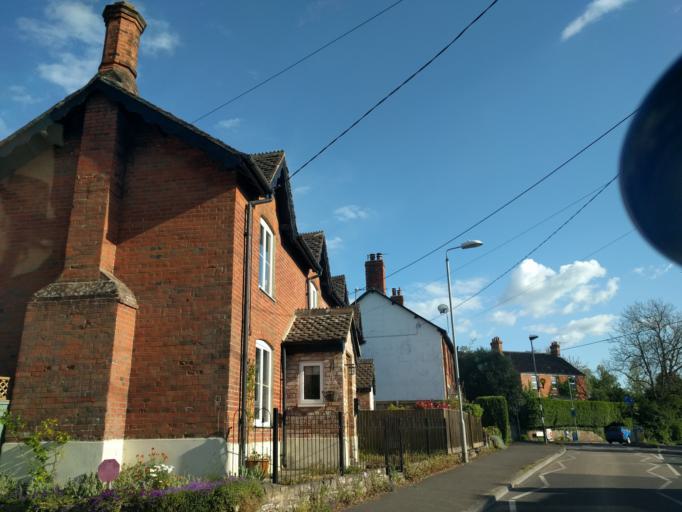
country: GB
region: England
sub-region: Wiltshire
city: Devizes
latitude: 51.3279
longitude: -2.0046
